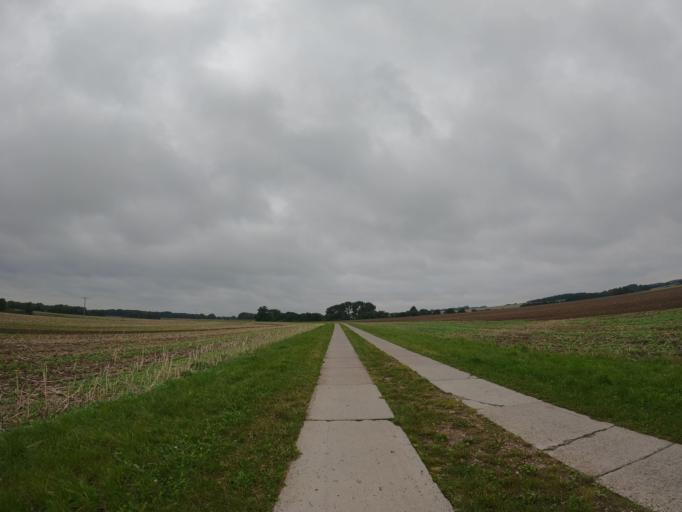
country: DE
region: Mecklenburg-Vorpommern
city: Poseritz
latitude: 54.2764
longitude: 13.2471
